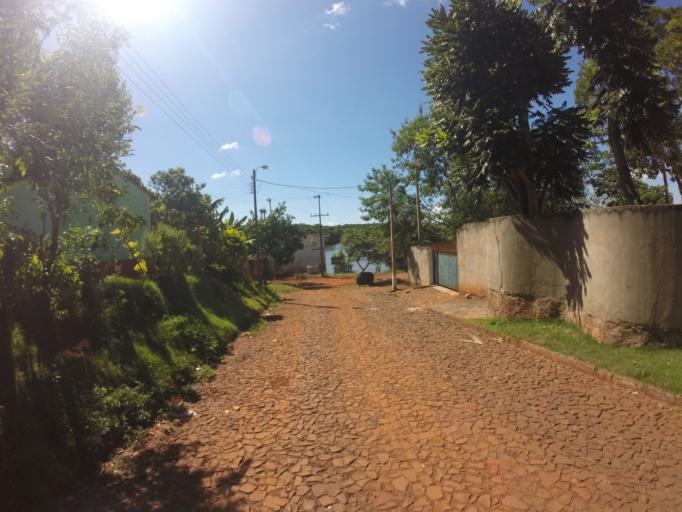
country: PY
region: Alto Parana
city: Ciudad del Este
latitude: -25.4426
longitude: -54.6421
